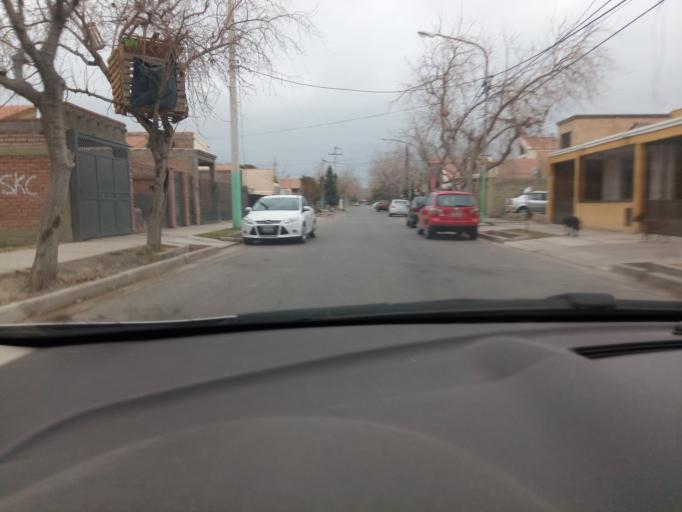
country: AR
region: San Juan
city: San Juan
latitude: -31.5350
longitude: -68.5950
